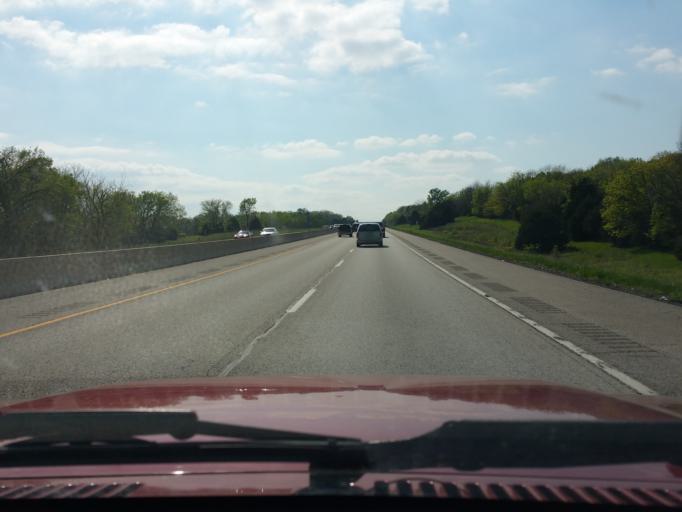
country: US
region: Kansas
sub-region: Douglas County
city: Lawrence
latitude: 38.9980
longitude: -95.3016
